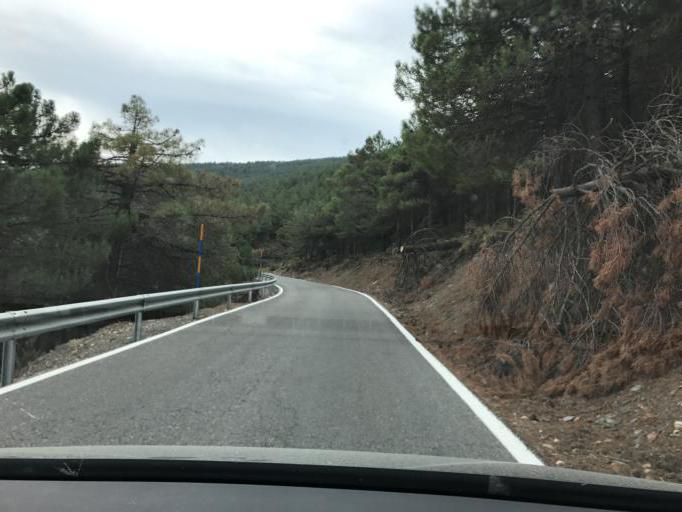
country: ES
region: Andalusia
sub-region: Provincia de Granada
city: Aldeire
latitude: 37.1311
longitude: -3.0437
